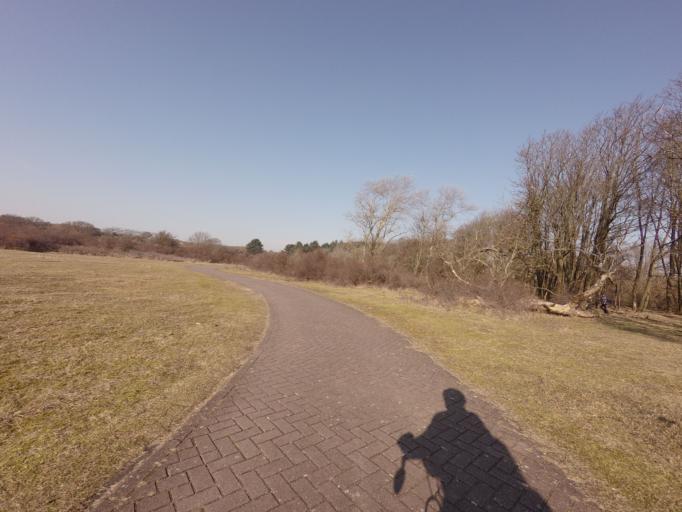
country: NL
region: North Holland
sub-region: Gemeente Bloemendaal
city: Bloemendaal
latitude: 52.4429
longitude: 4.6080
